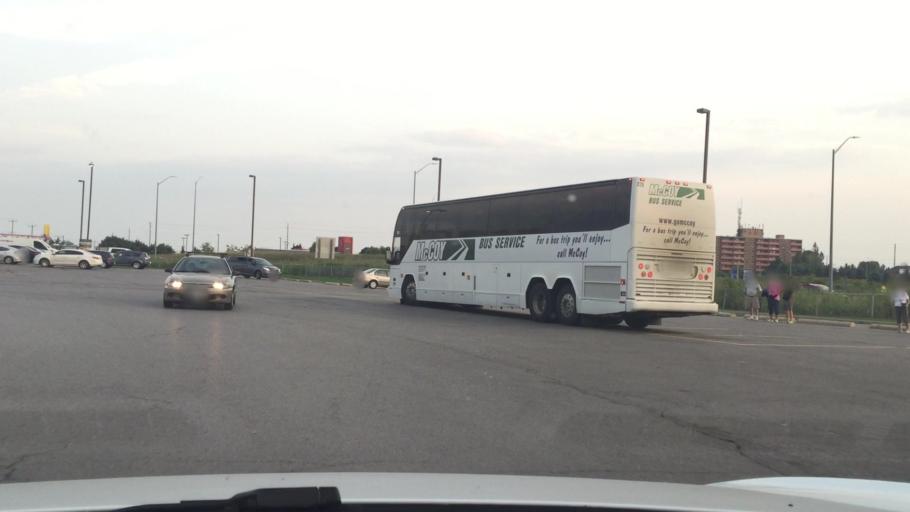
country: CA
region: Ontario
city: Cobourg
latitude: 43.9718
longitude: -78.2867
